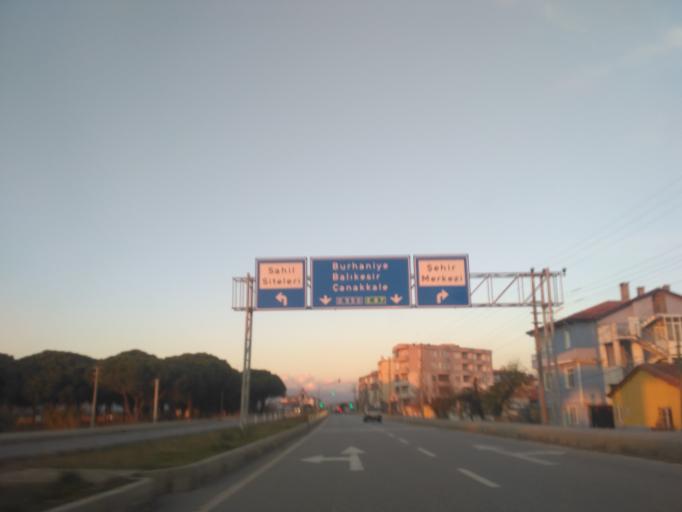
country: TR
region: Balikesir
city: Emrutabat
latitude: 39.3797
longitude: 26.8305
